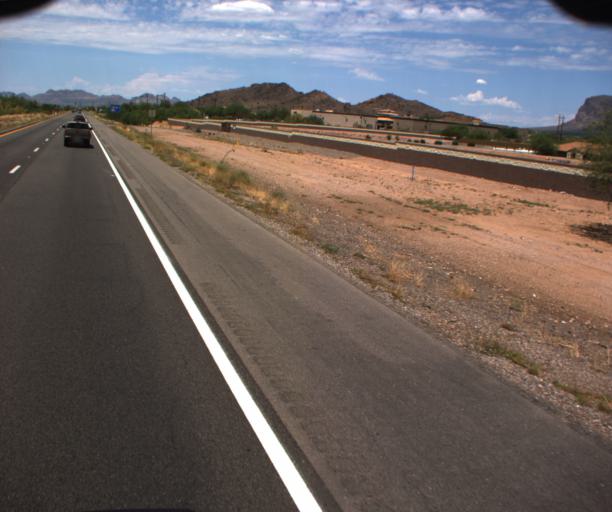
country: US
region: Arizona
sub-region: Pinal County
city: Apache Junction
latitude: 33.3632
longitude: -111.4742
